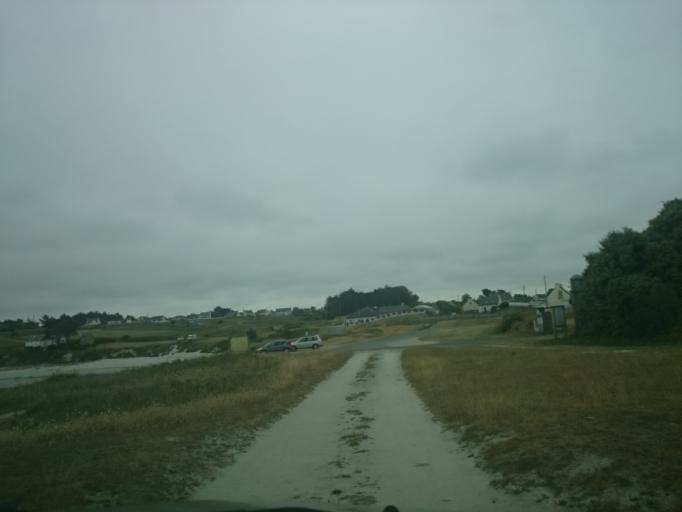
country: FR
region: Brittany
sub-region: Departement du Finistere
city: Saint-Pabu
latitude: 48.5768
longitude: -4.6268
